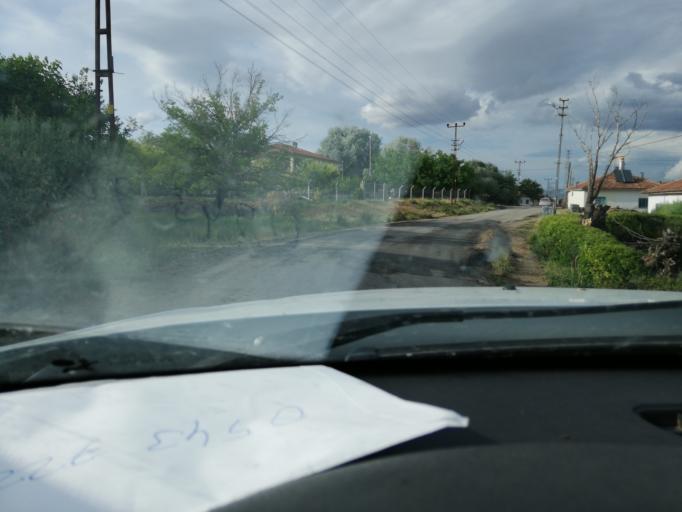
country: TR
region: Kirsehir
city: Kirsehir
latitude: 39.0254
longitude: 34.1250
